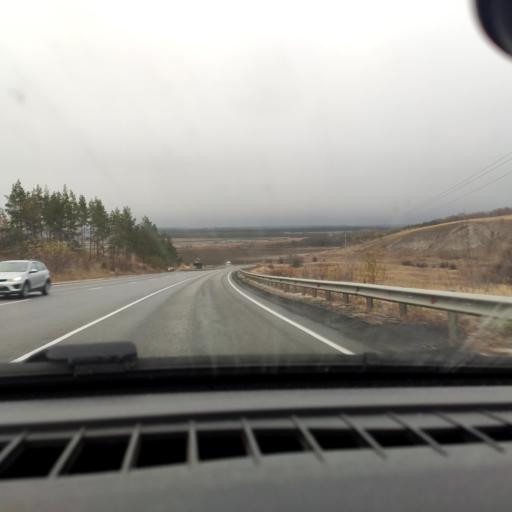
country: RU
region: Voronezj
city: Ostrogozhsk
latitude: 51.0231
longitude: 38.9826
